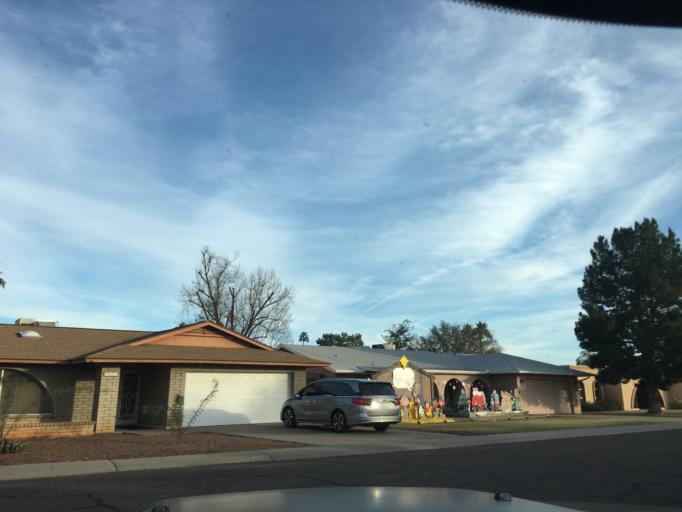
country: US
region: Arizona
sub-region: Maricopa County
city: Tempe
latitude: 33.3740
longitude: -111.9059
